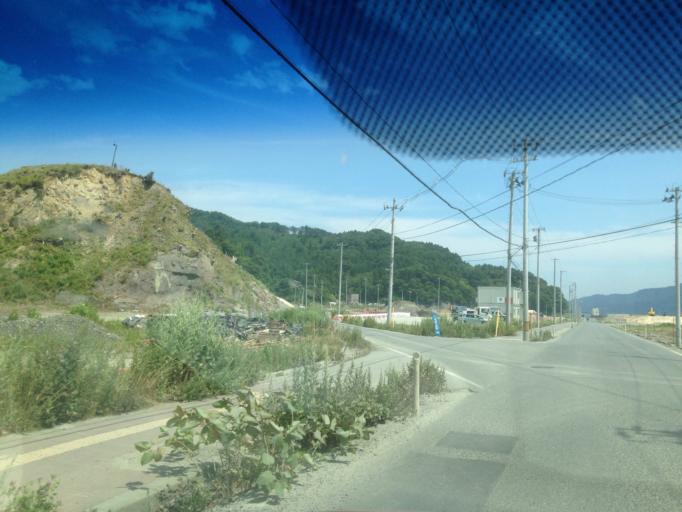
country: JP
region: Iwate
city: Otsuchi
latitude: 39.3596
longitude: 141.9134
